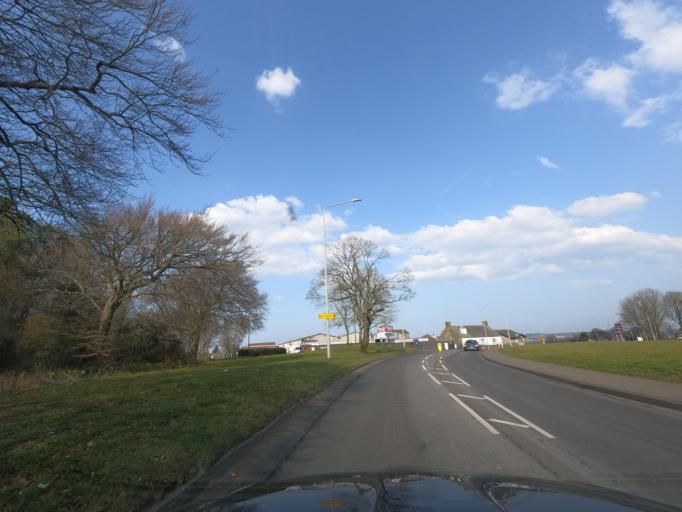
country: GB
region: Scotland
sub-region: West Lothian
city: Whitburn
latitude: 55.8602
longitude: -3.6896
